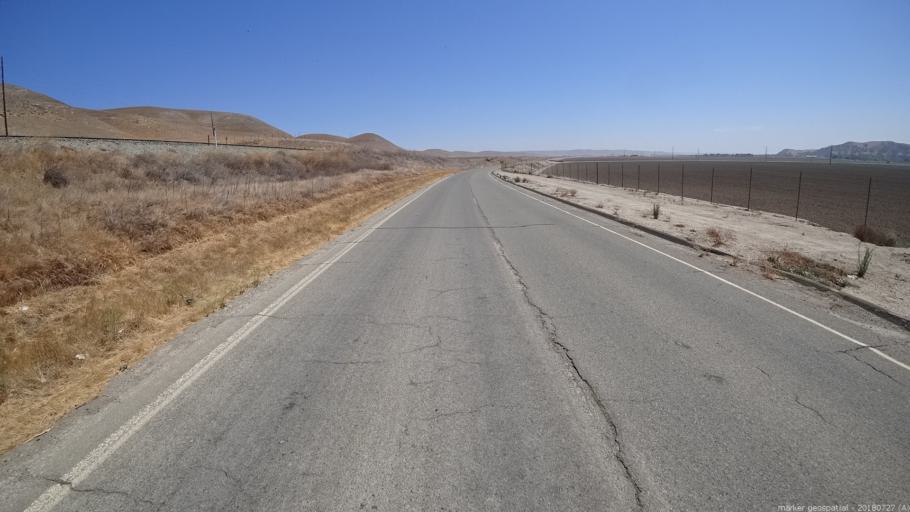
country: US
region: California
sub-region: Monterey County
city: King City
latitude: 36.1040
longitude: -120.9786
